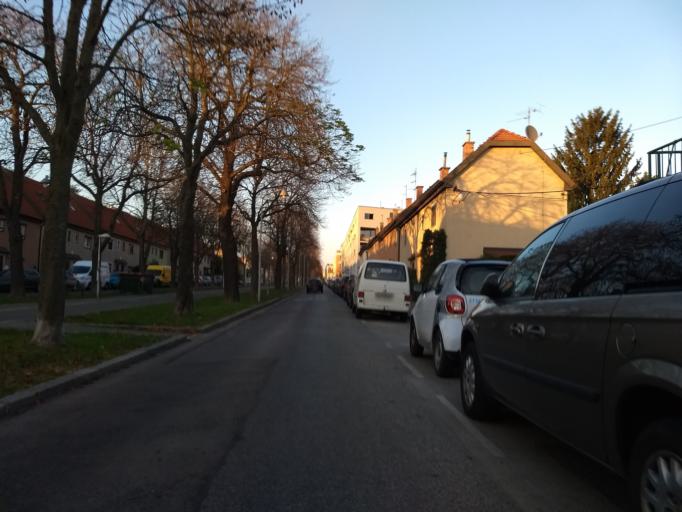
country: AT
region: Lower Austria
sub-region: Politischer Bezirk Modling
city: Vosendorf
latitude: 48.1646
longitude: 16.3235
